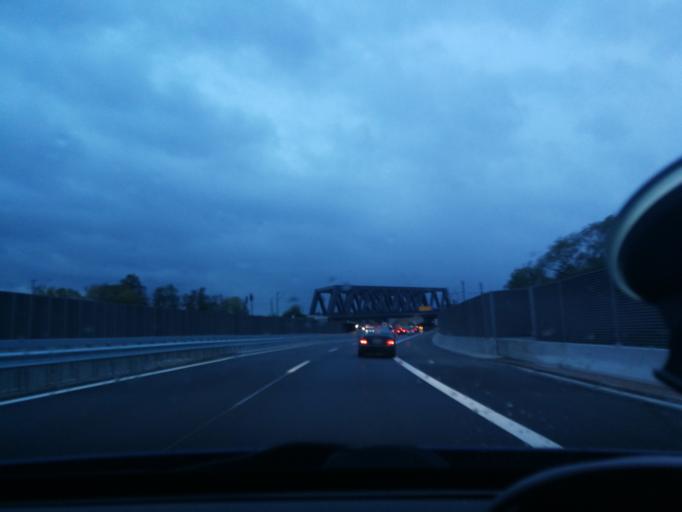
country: DE
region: Hamburg
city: Harburg
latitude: 53.4842
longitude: 10.0015
